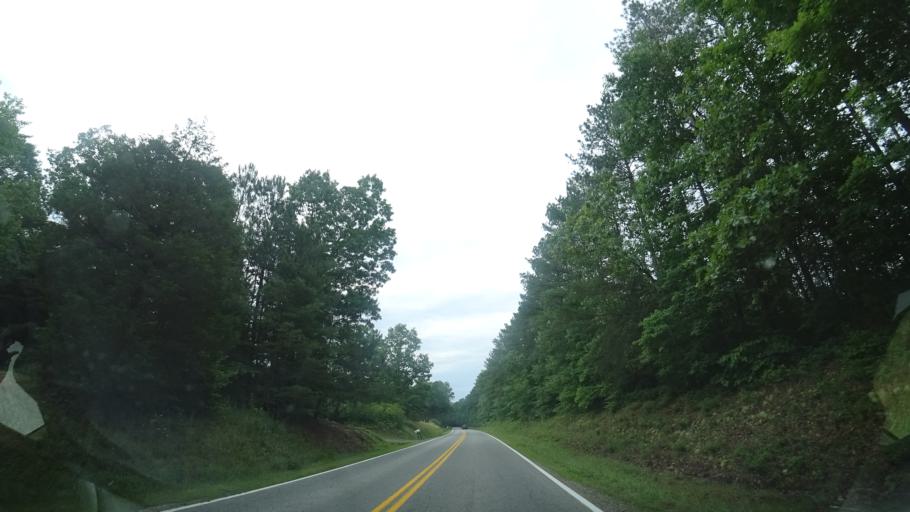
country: US
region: Virginia
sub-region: Louisa County
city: Louisa
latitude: 38.1418
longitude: -77.8118
